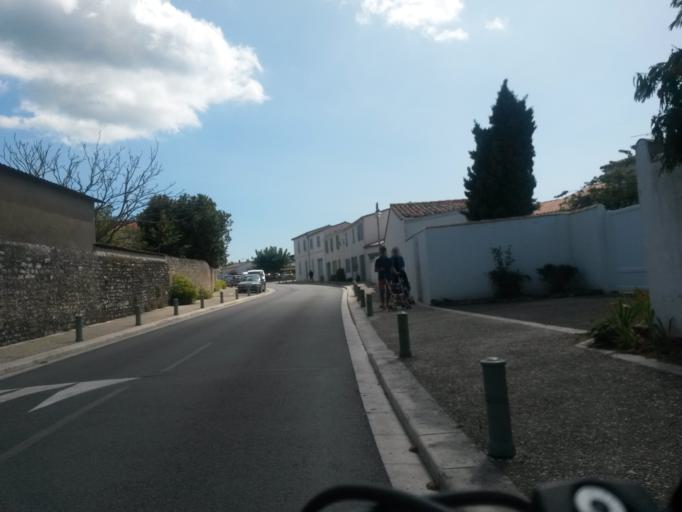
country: FR
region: Poitou-Charentes
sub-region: Departement de la Charente-Maritime
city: La Flotte
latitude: 46.1860
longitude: -1.3195
